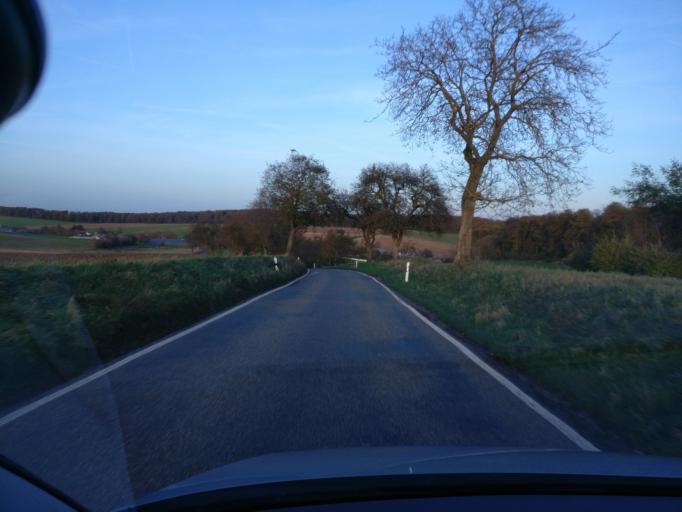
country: DE
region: Baden-Wuerttemberg
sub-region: Karlsruhe Region
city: Woessingen
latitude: 49.0397
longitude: 8.6037
